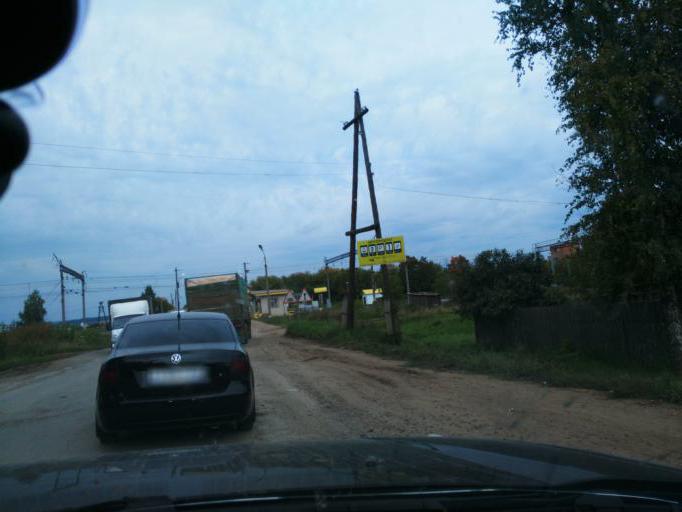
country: RU
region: Perm
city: Kuyeda
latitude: 56.4237
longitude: 55.5829
